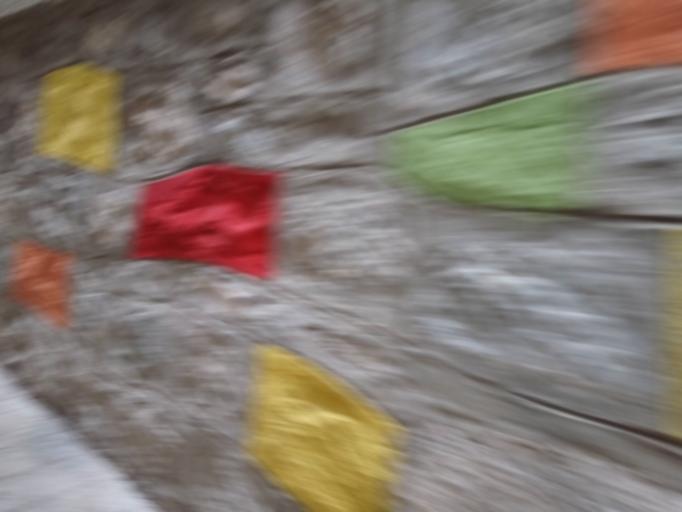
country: HR
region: Splitsko-Dalmatinska
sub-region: Grad Split
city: Split
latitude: 43.5107
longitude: 16.4327
